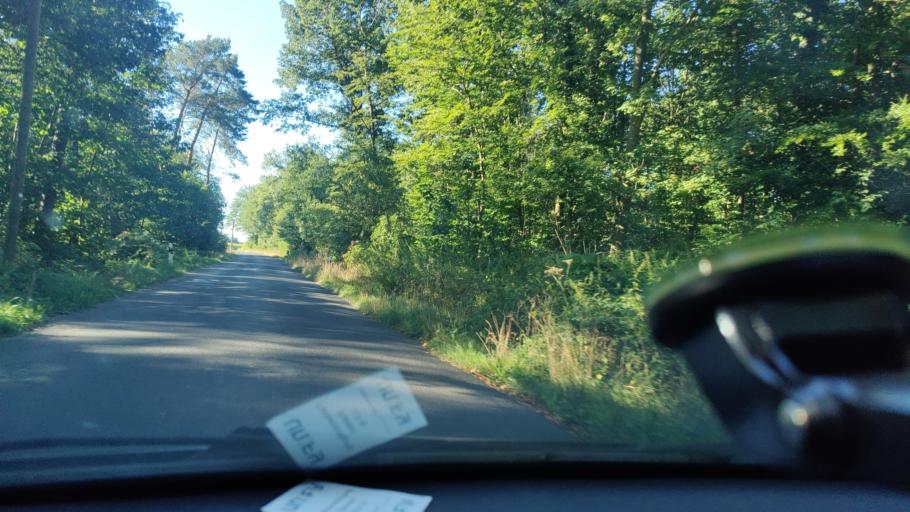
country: DE
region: North Rhine-Westphalia
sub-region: Regierungsbezirk Dusseldorf
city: Goch
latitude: 51.6650
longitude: 6.0832
